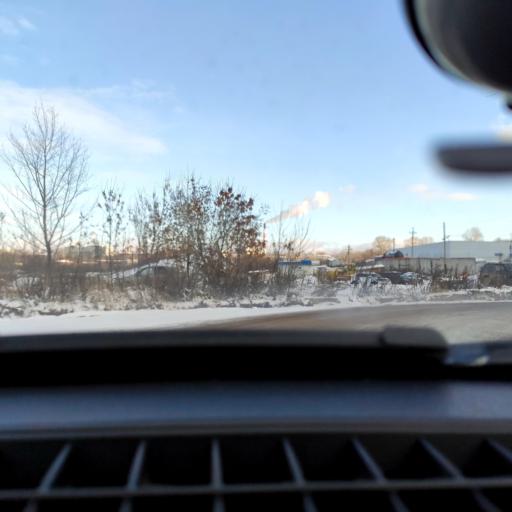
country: RU
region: Bashkortostan
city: Ufa
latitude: 54.8322
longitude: 56.0586
